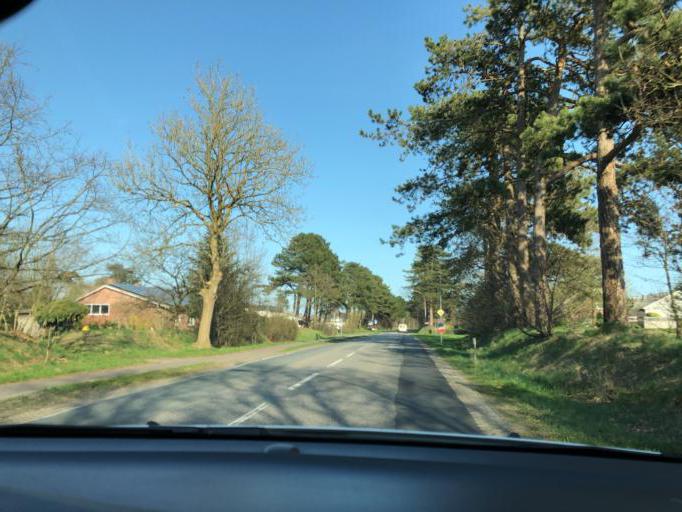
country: DE
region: Schleswig-Holstein
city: Bargum
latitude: 54.6901
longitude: 8.9652
